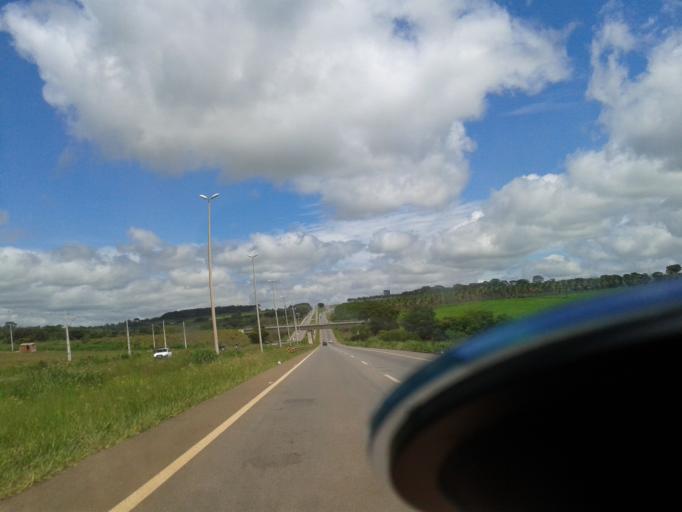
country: BR
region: Goias
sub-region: Goianira
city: Goianira
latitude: -16.4812
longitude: -49.4305
